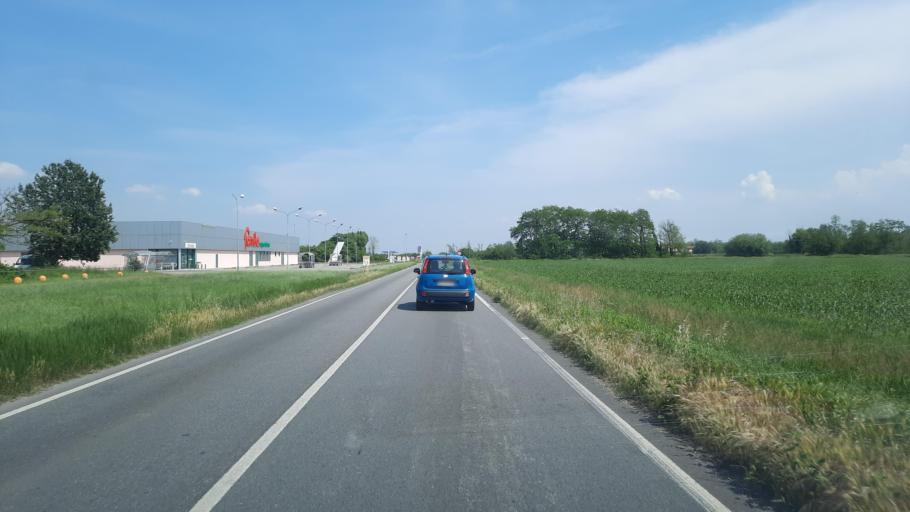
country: IT
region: Lombardy
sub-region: Provincia di Pavia
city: Carbonara al Ticino
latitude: 45.1587
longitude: 9.0830
